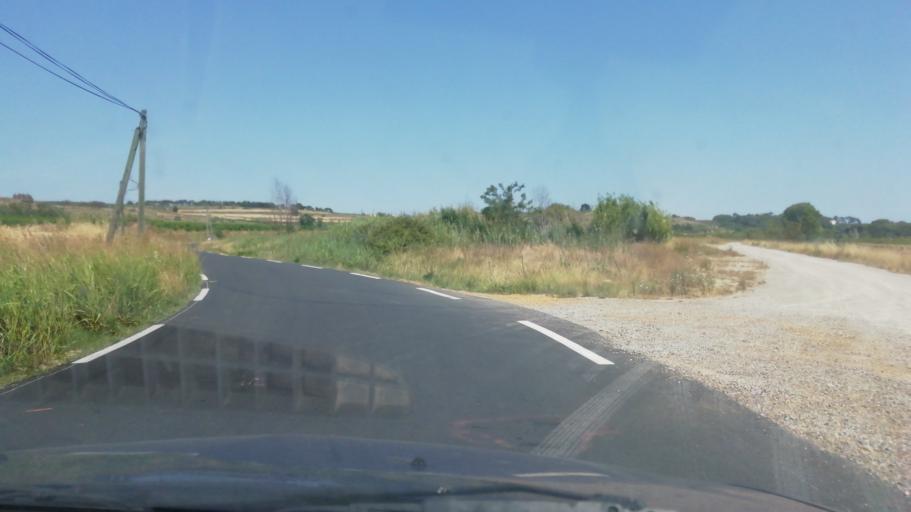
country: FR
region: Languedoc-Roussillon
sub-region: Departement de l'Herault
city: Capestang
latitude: 43.3315
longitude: 3.0565
